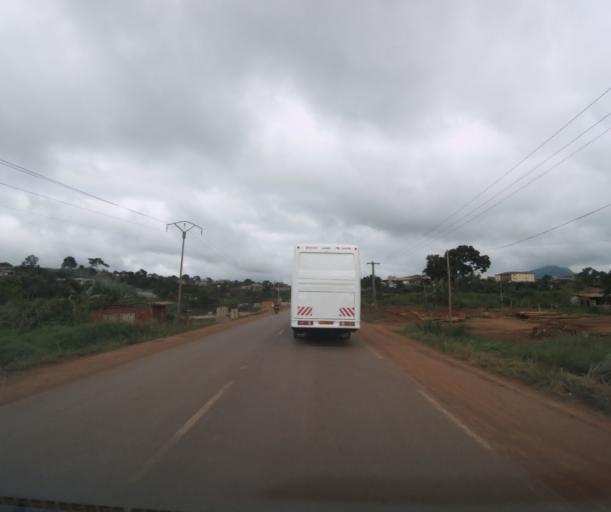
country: CM
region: Centre
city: Yaounde
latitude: 3.7947
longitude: 11.4834
